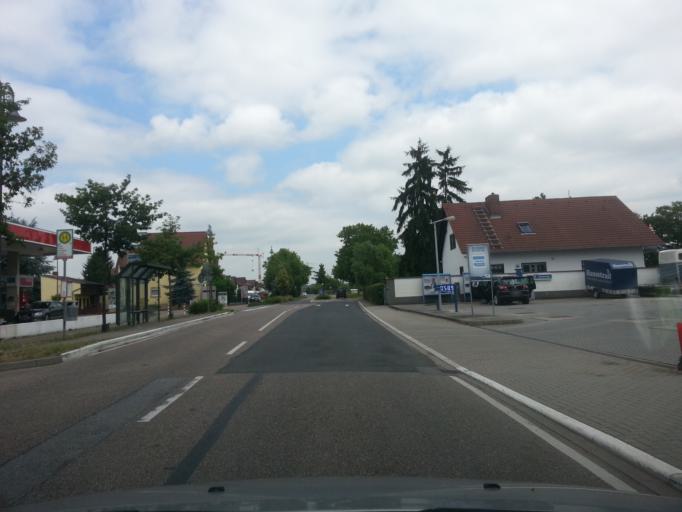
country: DE
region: Baden-Wuerttemberg
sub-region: Karlsruhe Region
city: Bruhl
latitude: 49.4023
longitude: 8.5378
